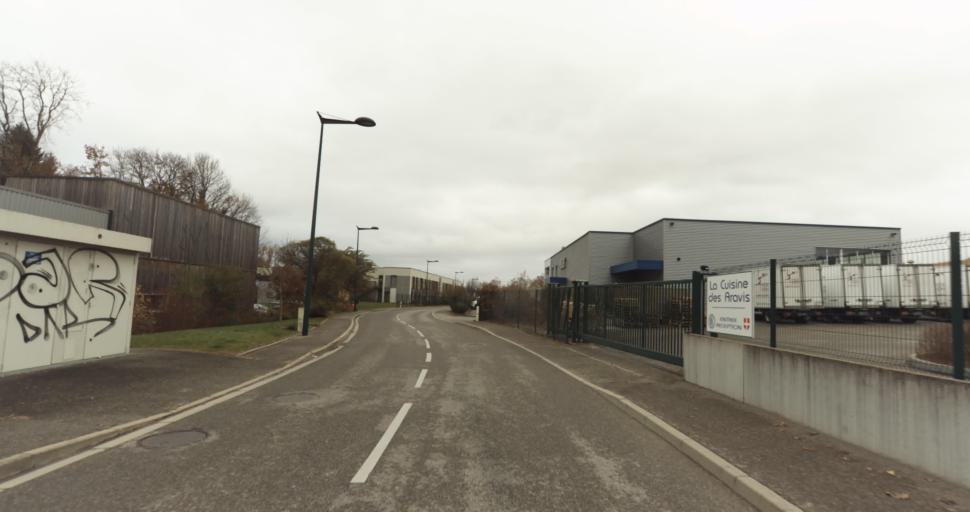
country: FR
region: Rhone-Alpes
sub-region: Departement de la Haute-Savoie
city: Saint-Martin-Bellevue
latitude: 45.9434
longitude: 6.1538
